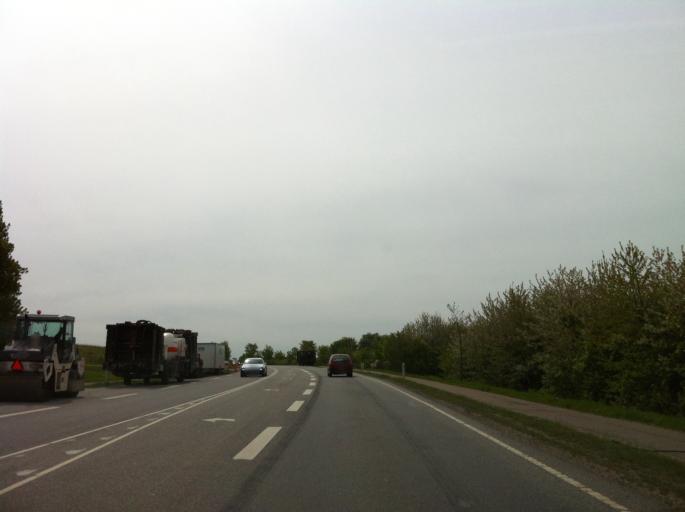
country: DK
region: Zealand
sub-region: Roskilde Kommune
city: Jyllinge
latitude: 55.7170
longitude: 12.1122
